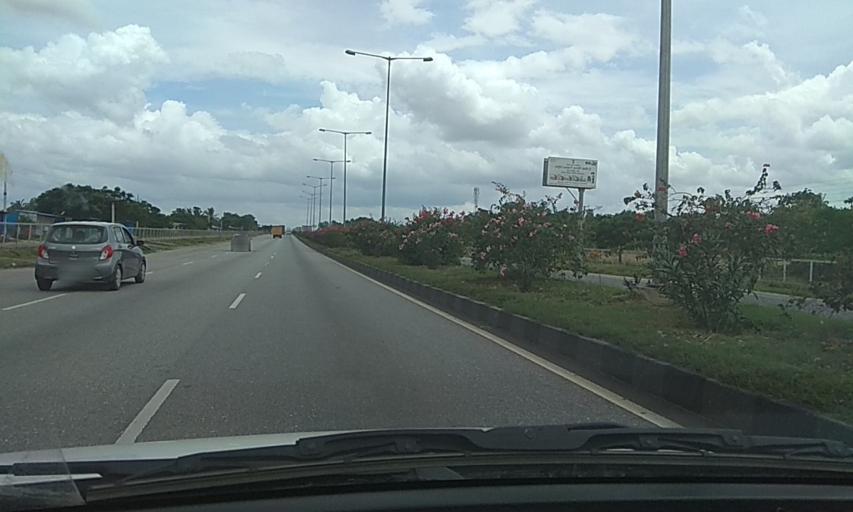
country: IN
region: Karnataka
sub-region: Tumkur
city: Sira
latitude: 13.6088
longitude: 76.9567
